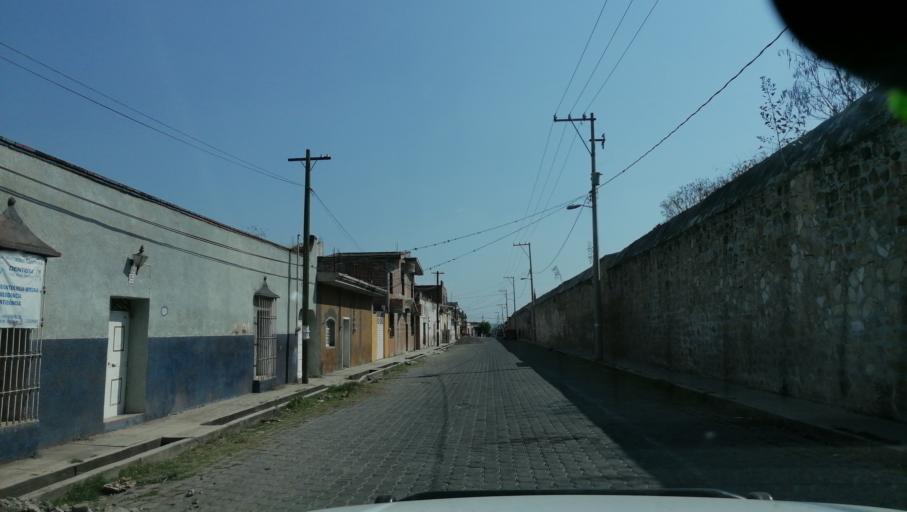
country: MX
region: Puebla
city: Huaquechula
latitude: 18.7702
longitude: -98.5395
